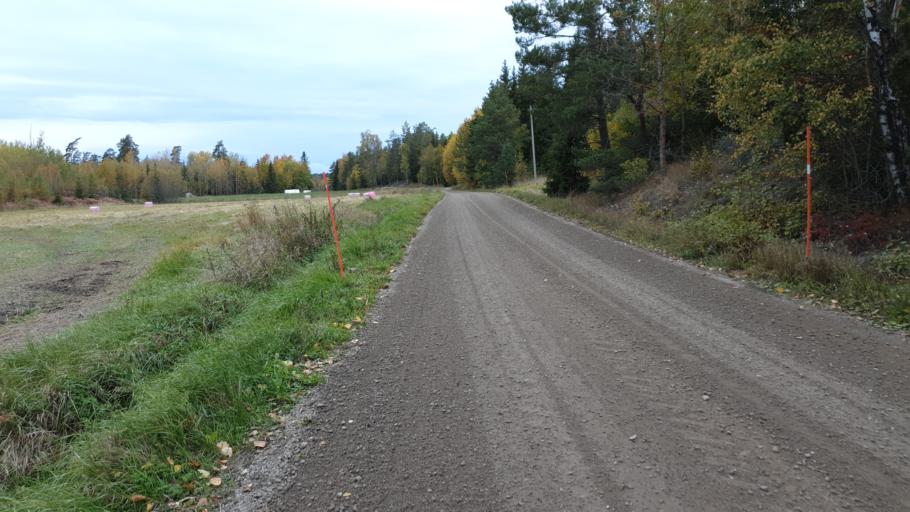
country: SE
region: Vaestmanland
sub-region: Sala Kommun
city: Sala
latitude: 59.8185
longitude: 16.6523
